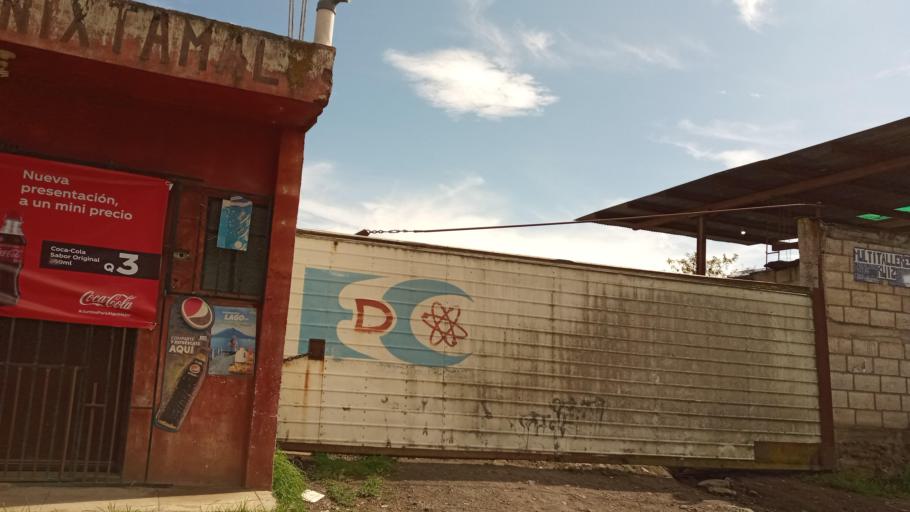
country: GT
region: Quetzaltenango
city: Quetzaltenango
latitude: 14.8467
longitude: -91.5104
